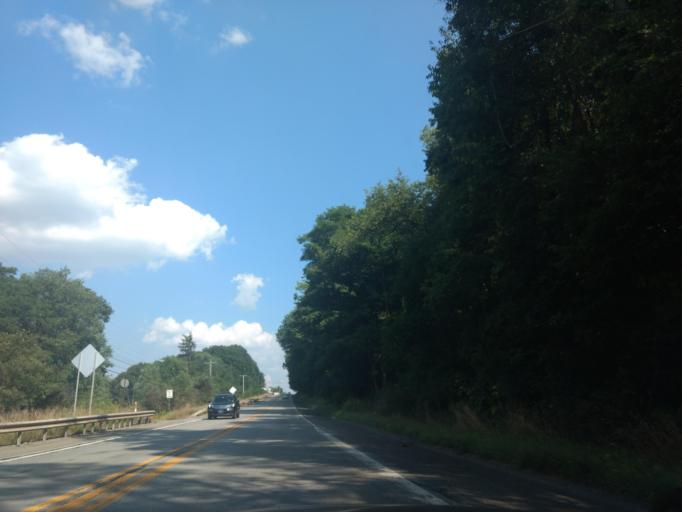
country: US
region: Pennsylvania
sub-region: Butler County
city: Zelienople
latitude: 40.8005
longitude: -80.1142
